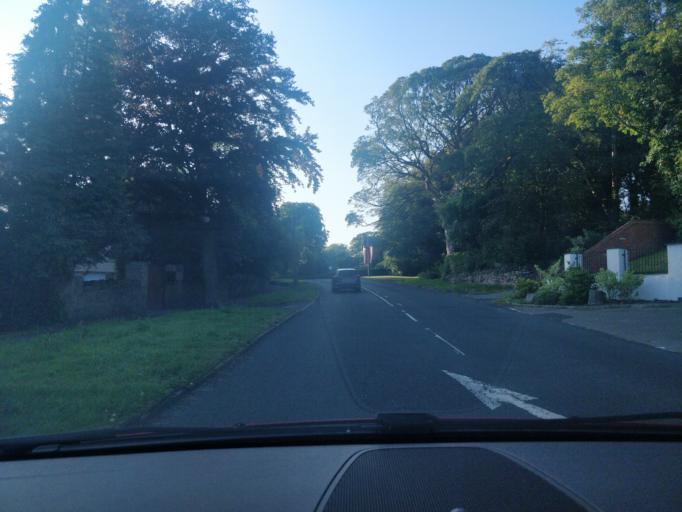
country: GB
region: England
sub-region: Lancashire
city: Parbold
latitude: 53.5959
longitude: -2.7663
